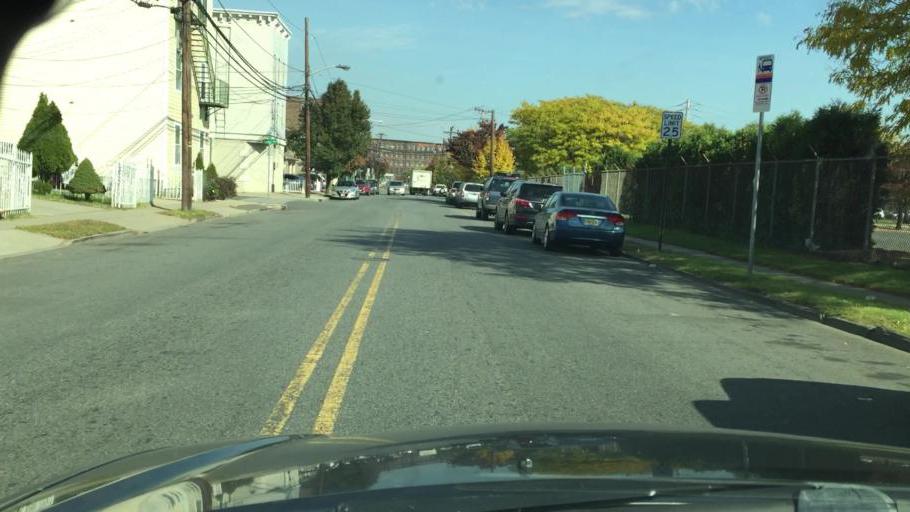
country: US
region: New Jersey
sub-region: Union County
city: Elizabeth
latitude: 40.6522
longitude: -74.1804
